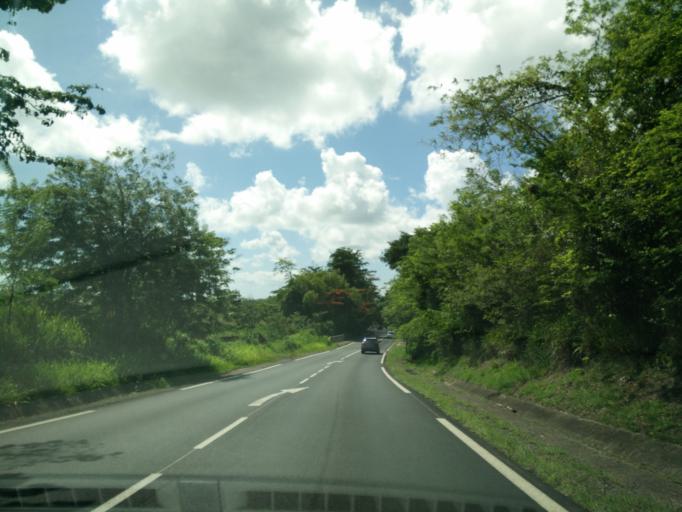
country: MQ
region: Martinique
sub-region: Martinique
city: Les Trois-Ilets
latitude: 14.5305
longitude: -61.0214
